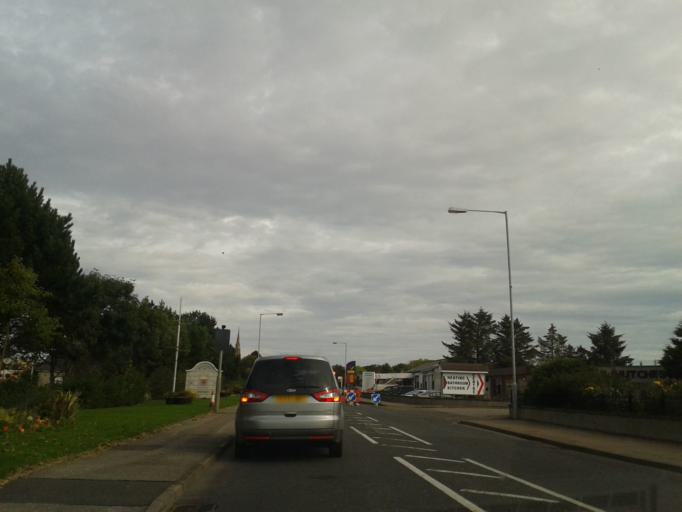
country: GB
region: Scotland
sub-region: Aberdeenshire
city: Portsoy
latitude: 57.6789
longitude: -2.6987
